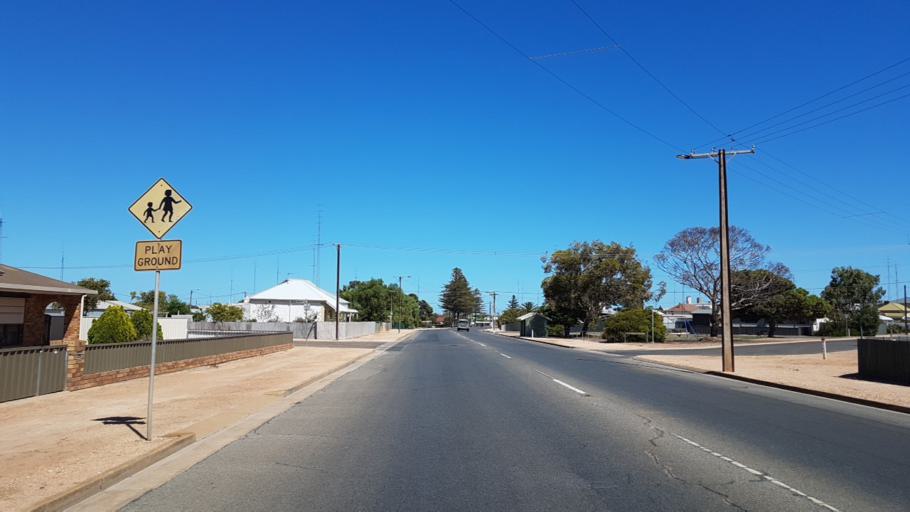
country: AU
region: South Australia
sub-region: Copper Coast
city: Wallaroo
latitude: -33.9348
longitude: 137.6359
